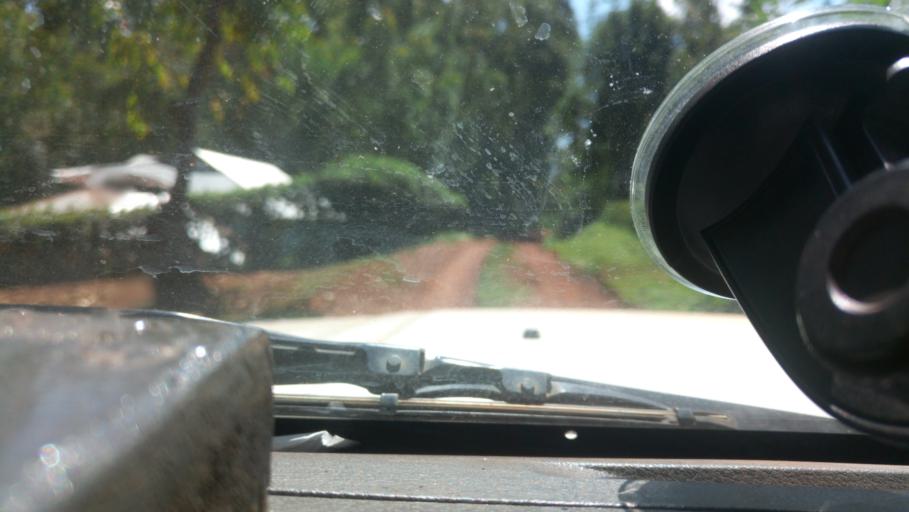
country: KE
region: Kisii
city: Ogembo
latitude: -0.8689
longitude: 34.7356
